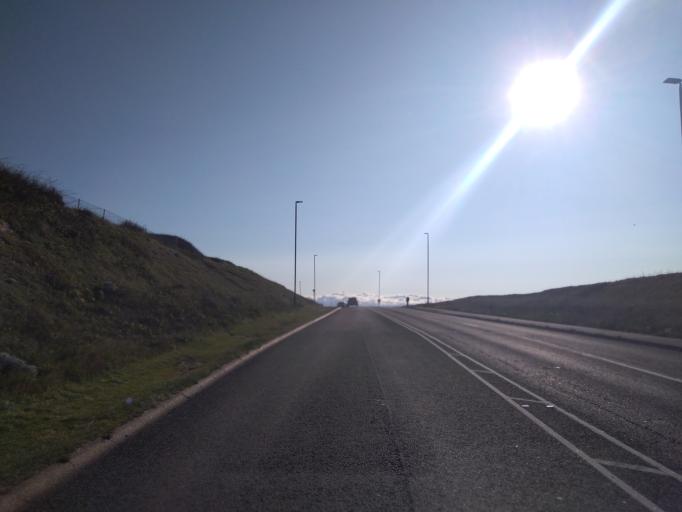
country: GB
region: England
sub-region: East Sussex
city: Peacehaven
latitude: 50.7981
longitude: -0.0310
